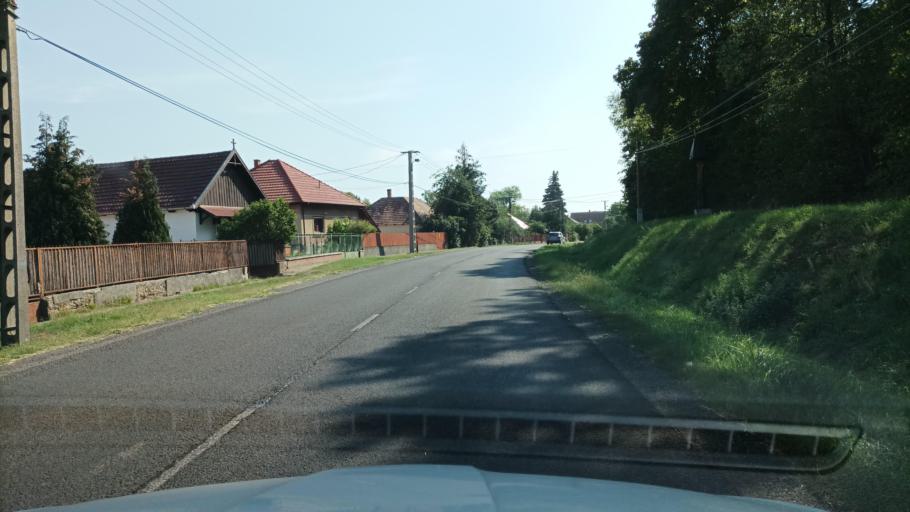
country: HU
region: Pest
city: Valko
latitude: 47.5677
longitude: 19.4887
